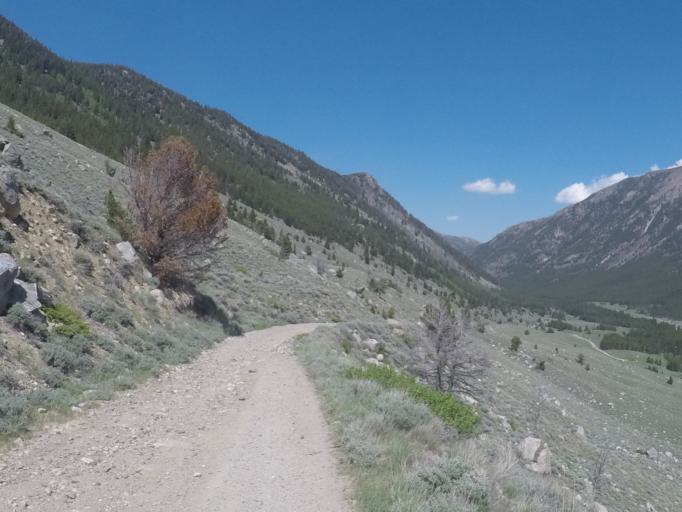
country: US
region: Montana
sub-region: Carbon County
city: Red Lodge
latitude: 45.0579
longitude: -109.4215
